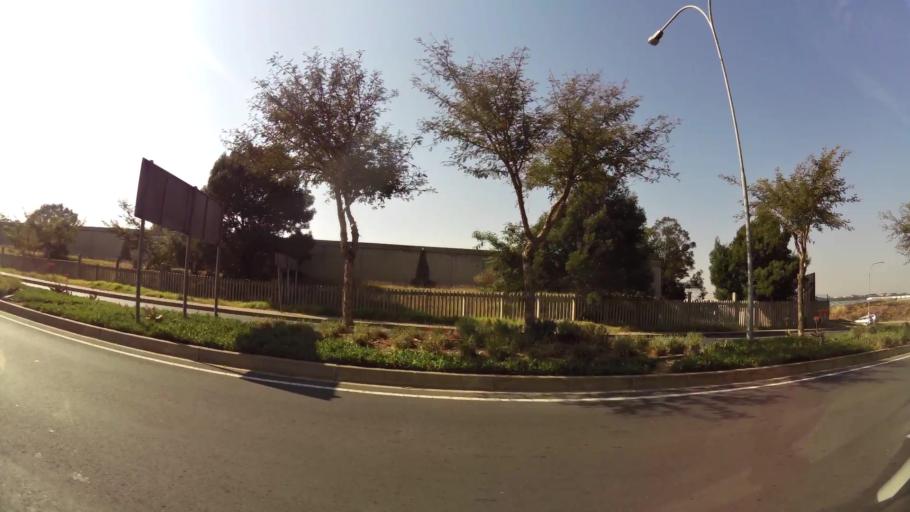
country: ZA
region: Gauteng
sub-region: City of Johannesburg Metropolitan Municipality
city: Modderfontein
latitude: -26.1035
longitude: 28.1323
